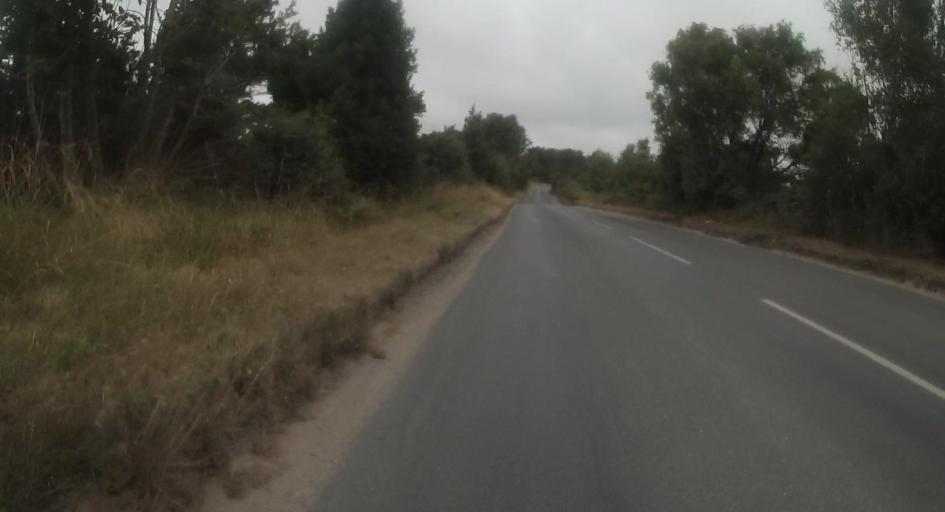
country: GB
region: England
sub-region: Dorset
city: Wool
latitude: 50.6922
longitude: -2.1706
